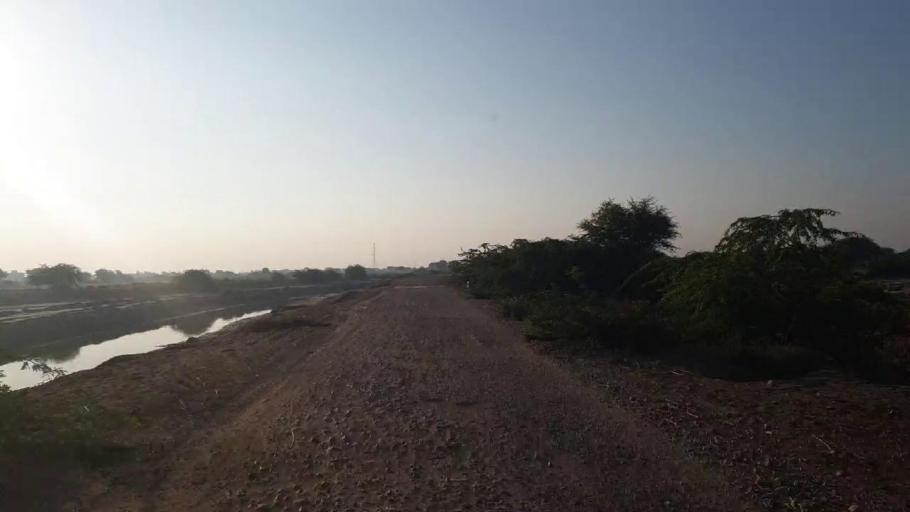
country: PK
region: Sindh
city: Badin
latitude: 24.6557
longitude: 68.7889
